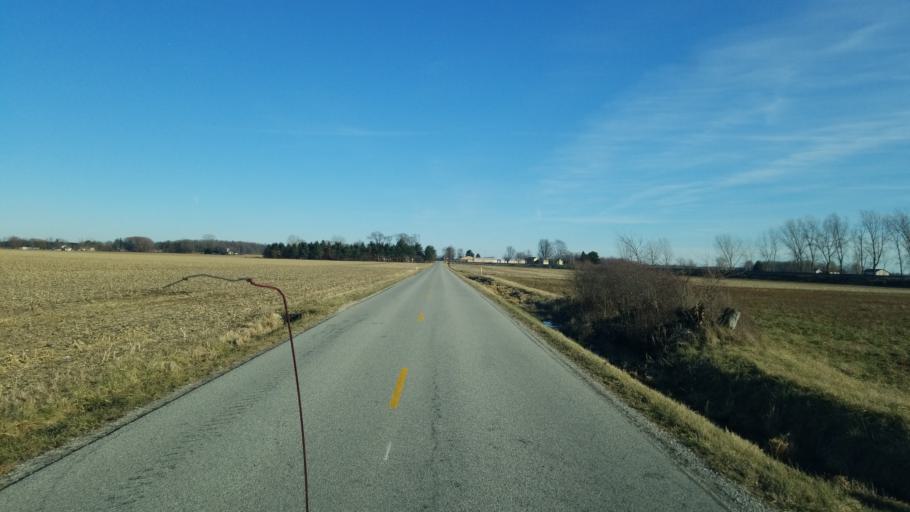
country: US
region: Ohio
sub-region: Sandusky County
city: Green Springs
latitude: 41.2562
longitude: -83.0214
